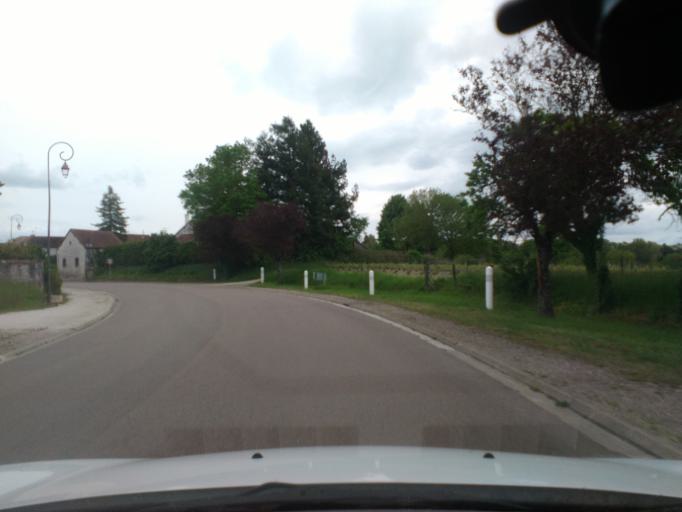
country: FR
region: Champagne-Ardenne
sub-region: Departement de l'Aube
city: Bar-sur-Aube
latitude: 48.2246
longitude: 4.8041
